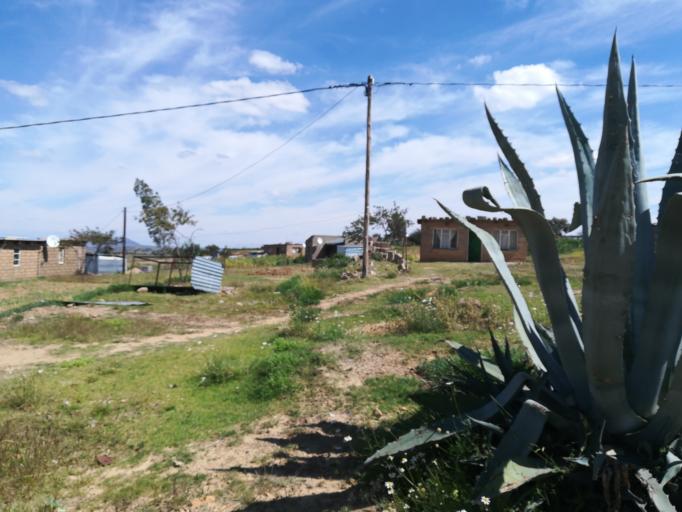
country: LS
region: Mohale's Hoek District
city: Mohale's Hoek
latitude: -30.1033
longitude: 27.4698
